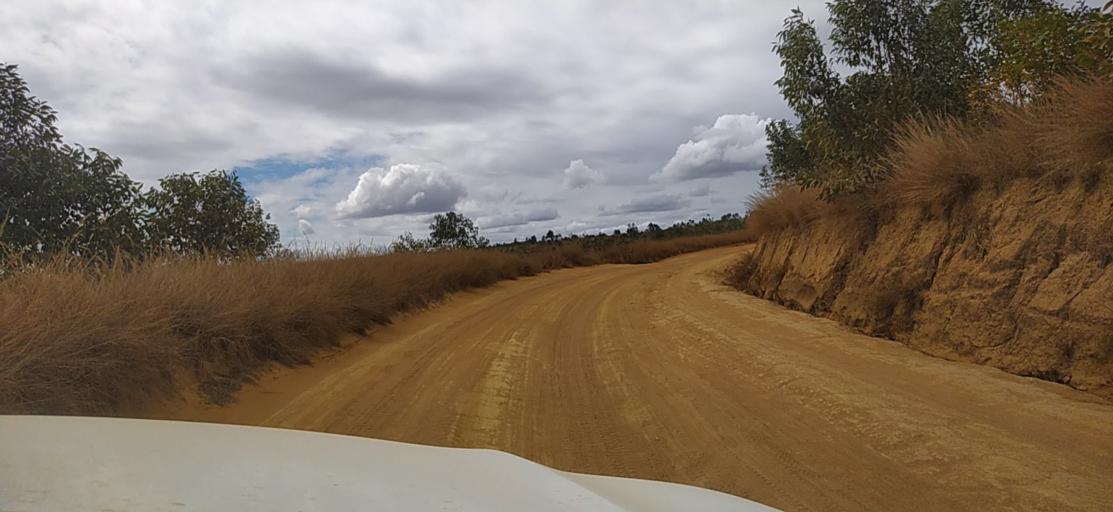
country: MG
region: Alaotra Mangoro
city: Ambatondrazaka
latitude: -17.9524
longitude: 48.2485
